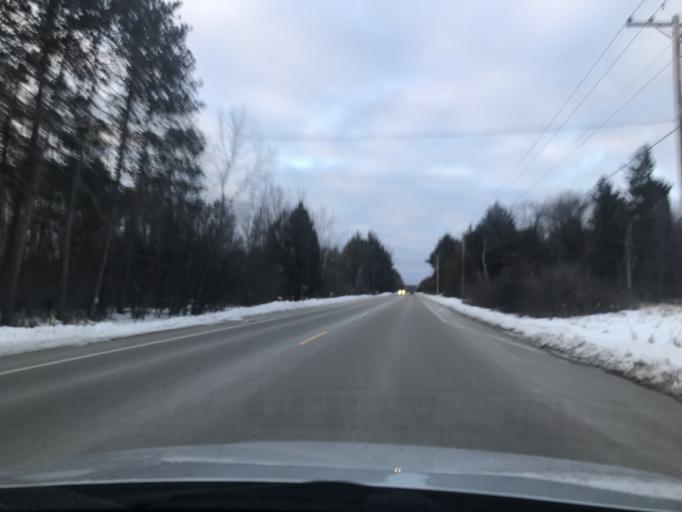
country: US
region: Wisconsin
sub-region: Marinette County
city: Marinette
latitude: 45.1284
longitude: -87.6861
